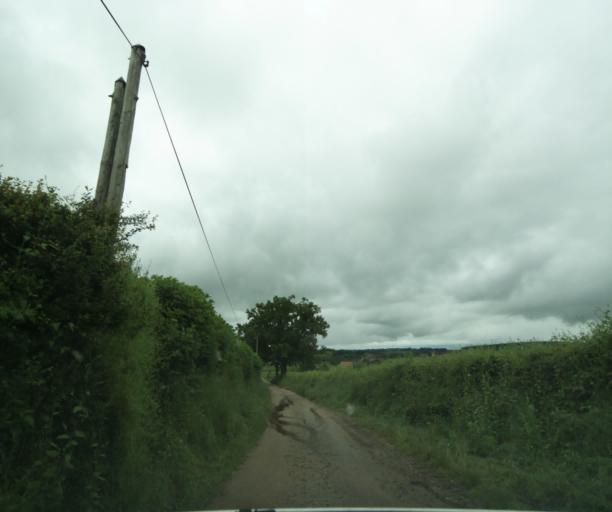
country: FR
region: Bourgogne
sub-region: Departement de Saone-et-Loire
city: Charolles
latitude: 46.4749
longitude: 4.3502
